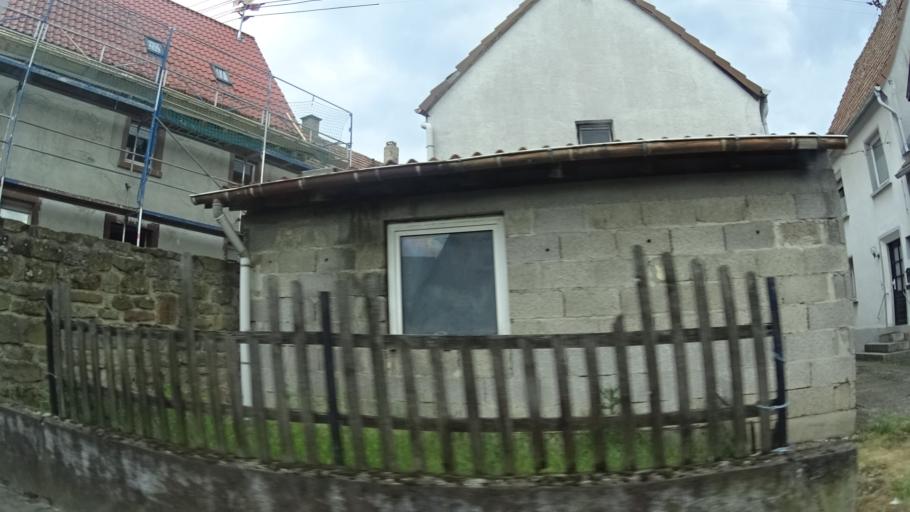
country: DE
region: Rheinland-Pfalz
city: Lustadt
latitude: 49.2437
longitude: 8.2700
